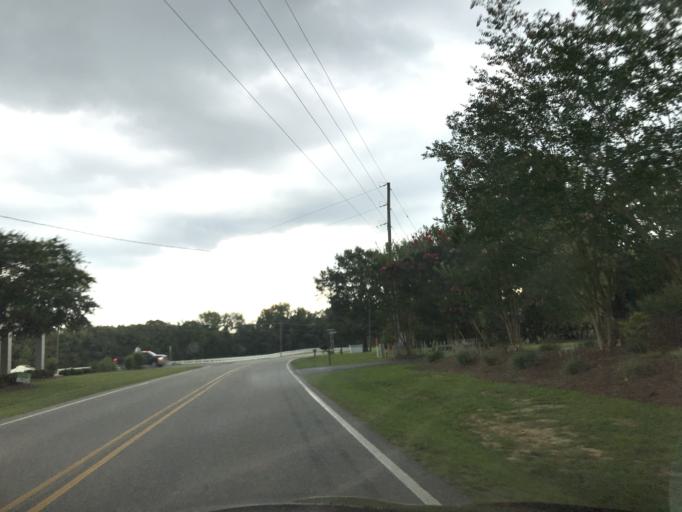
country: US
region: North Carolina
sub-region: Johnston County
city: Wilsons Mills
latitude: 35.5365
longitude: -78.4247
